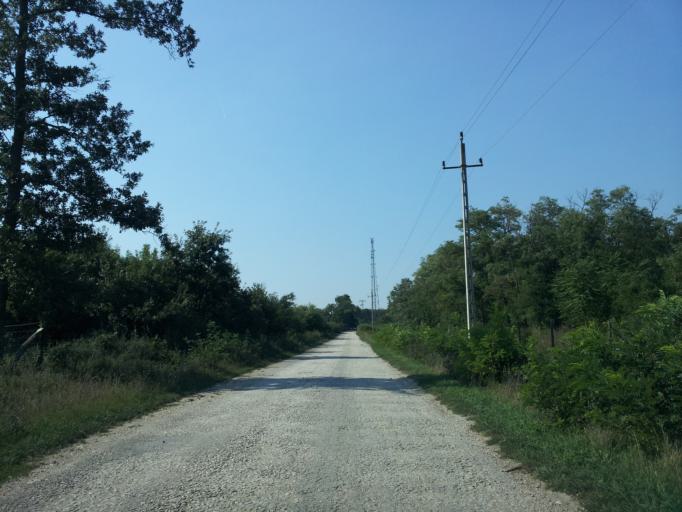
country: HU
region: Fejer
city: Polgardi
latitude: 47.0274
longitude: 18.2773
